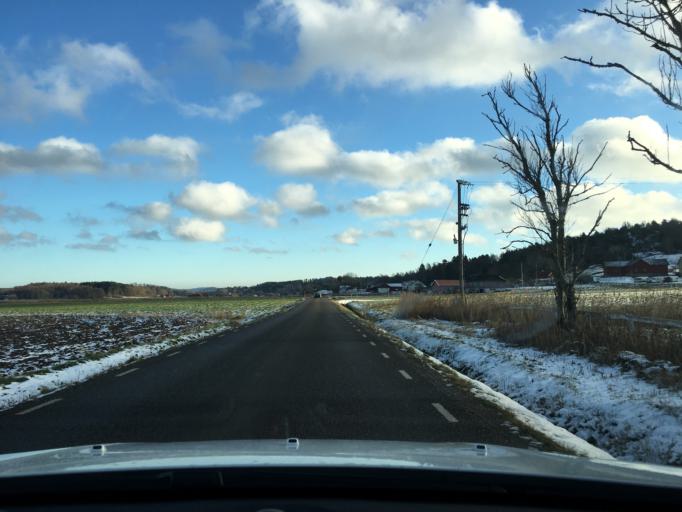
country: SE
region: Vaestra Goetaland
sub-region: Tjorns Kommun
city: Myggenas
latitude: 58.0492
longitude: 11.7164
